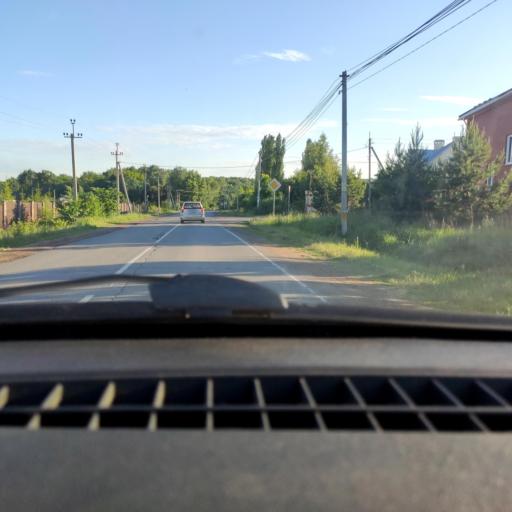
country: RU
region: Bashkortostan
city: Avdon
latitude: 54.6417
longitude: 55.7025
